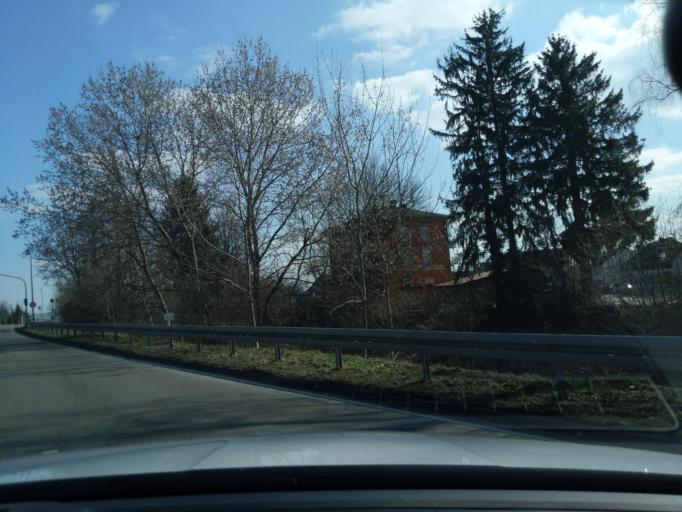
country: DE
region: Bavaria
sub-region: Swabia
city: Vohringen
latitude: 48.3178
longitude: 10.1023
